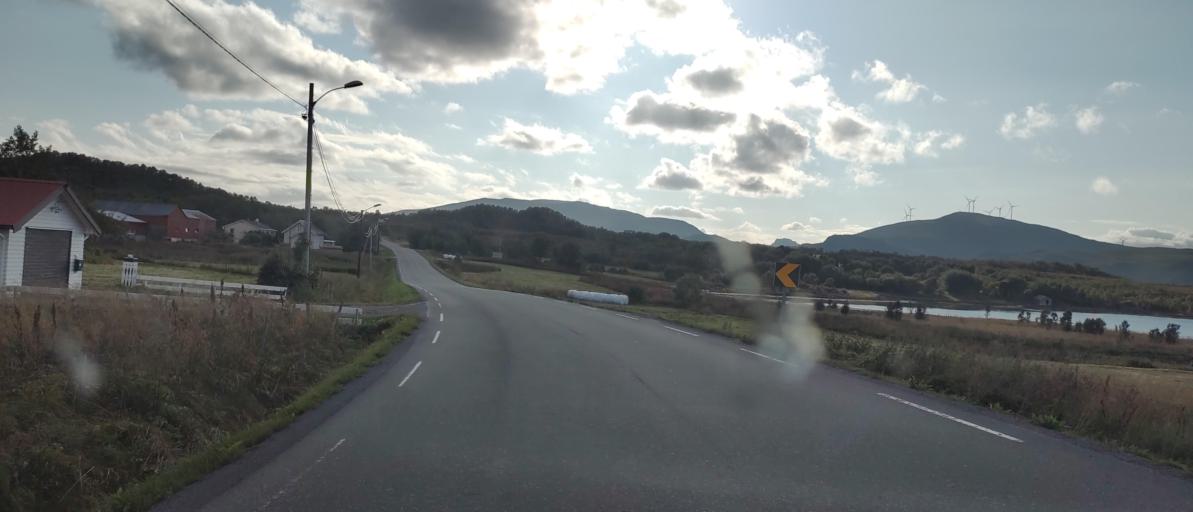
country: NO
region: Nordland
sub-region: Sortland
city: Sortland
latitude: 68.7251
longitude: 15.4762
